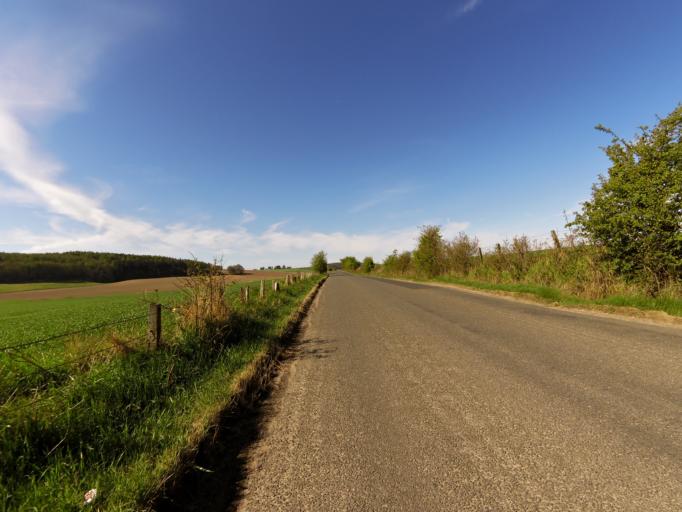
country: GB
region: Scotland
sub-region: Dundee City
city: Dundee
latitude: 56.4114
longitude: -2.9919
